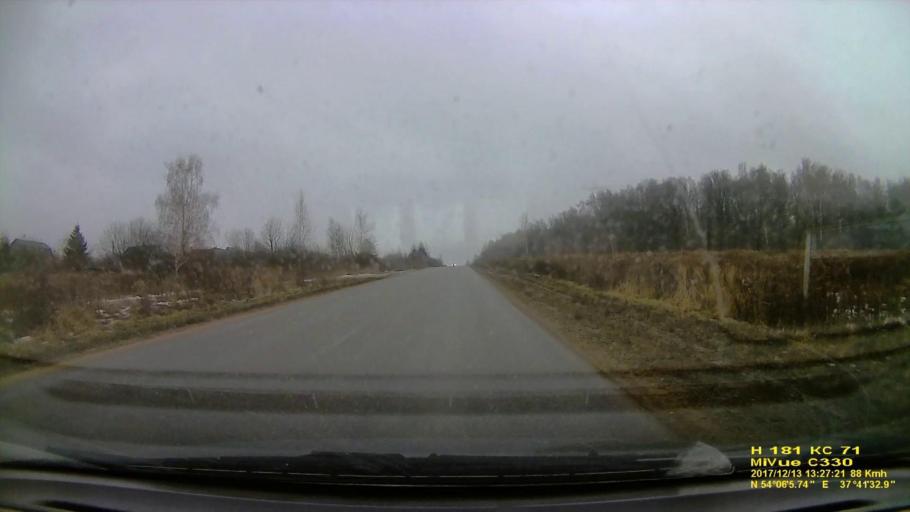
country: RU
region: Tula
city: Skuratovskiy
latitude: 54.1014
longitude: 37.6925
